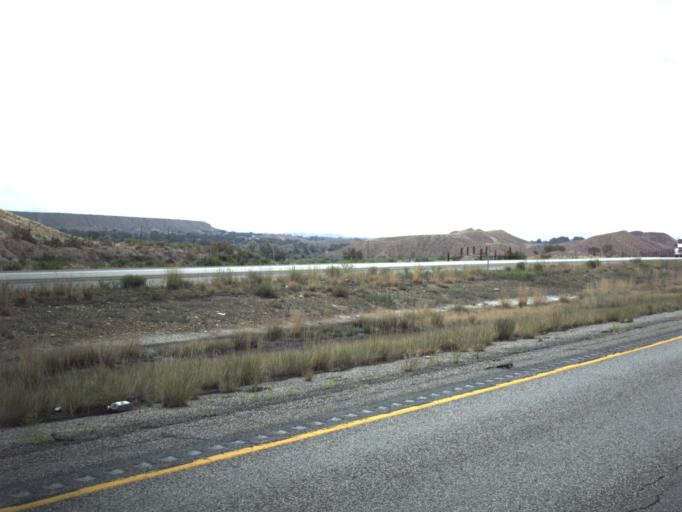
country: US
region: Utah
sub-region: Carbon County
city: Carbonville
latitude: 39.6293
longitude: -110.8618
